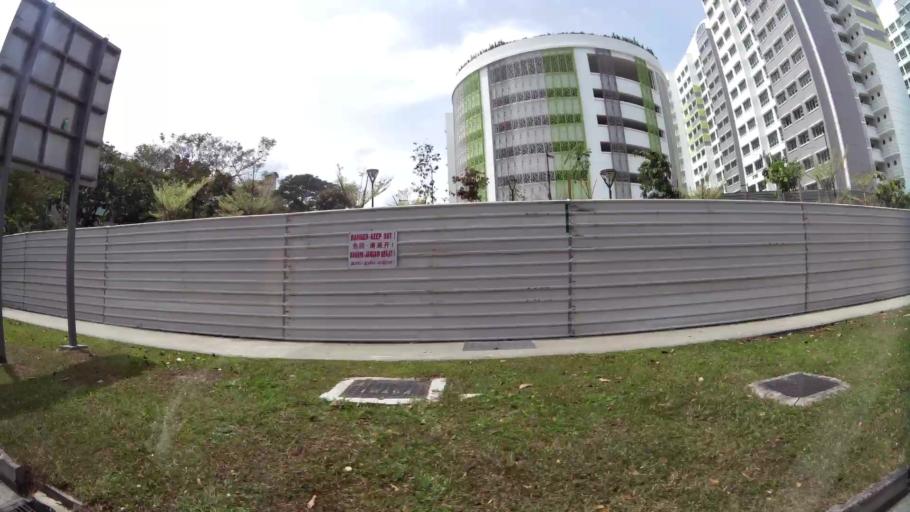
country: MY
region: Johor
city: Johor Bahru
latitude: 1.3504
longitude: 103.7128
